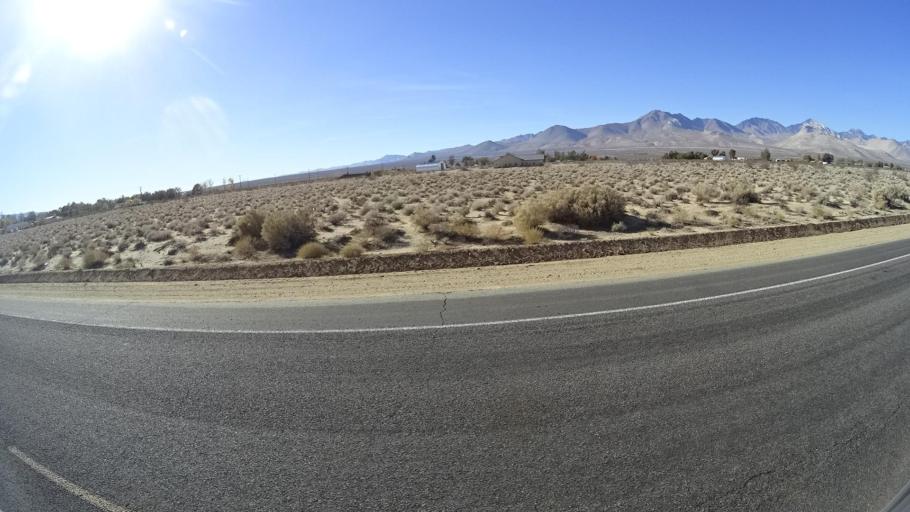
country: US
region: California
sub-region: Kern County
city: Inyokern
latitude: 35.6327
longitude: -117.8082
